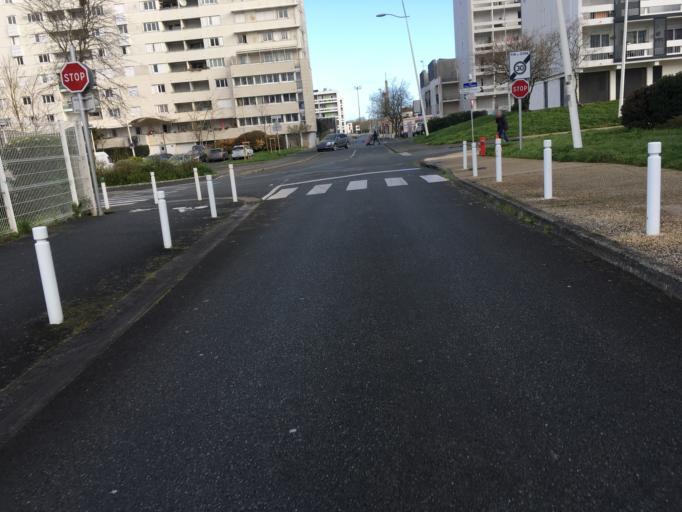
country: FR
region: Poitou-Charentes
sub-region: Departement de la Charente-Maritime
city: La Rochelle
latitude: 46.1689
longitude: -1.1775
